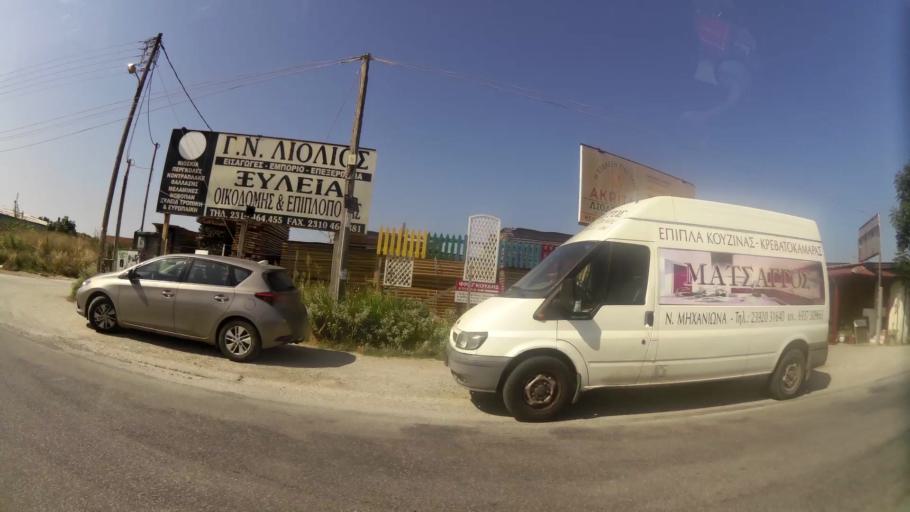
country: GR
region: Central Macedonia
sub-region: Nomos Thessalonikis
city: Neo Rysi
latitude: 40.5125
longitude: 22.9880
